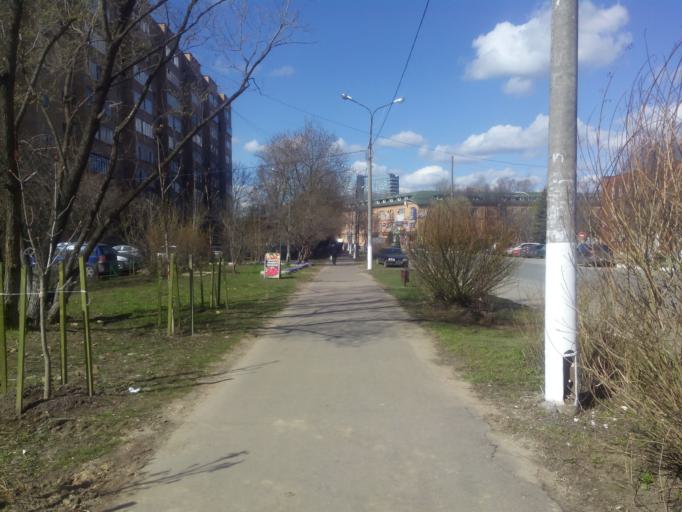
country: RU
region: Moskovskaya
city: Odintsovo
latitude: 55.6715
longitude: 37.2875
